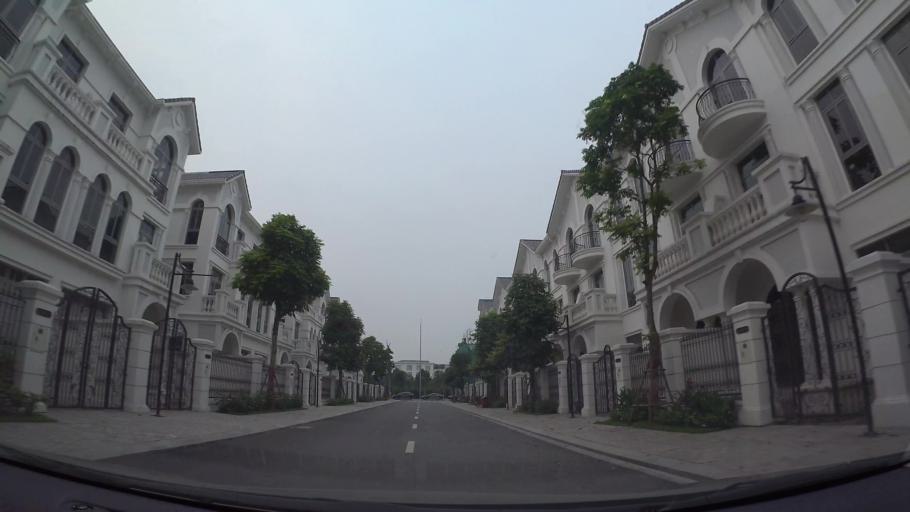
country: VN
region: Ha Noi
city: Trau Quy
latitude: 21.0502
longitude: 105.9061
